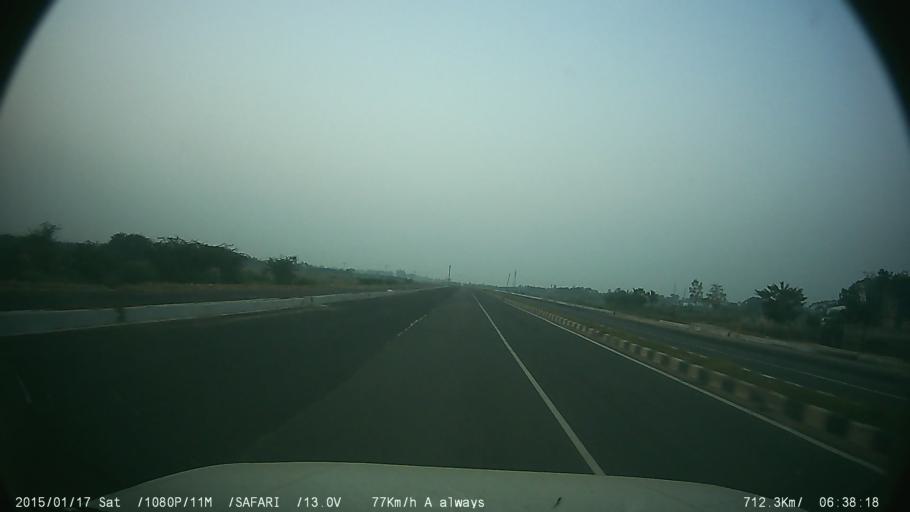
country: IN
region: Tamil Nadu
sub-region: Kancheepuram
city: Sriperumbudur
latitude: 12.9373
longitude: 79.9355
